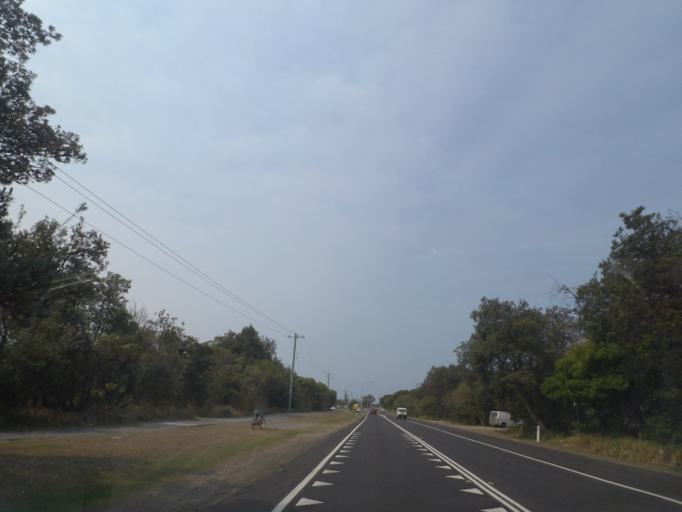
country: AU
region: New South Wales
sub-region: Tweed
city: Casuarina
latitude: -28.3403
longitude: 153.5721
